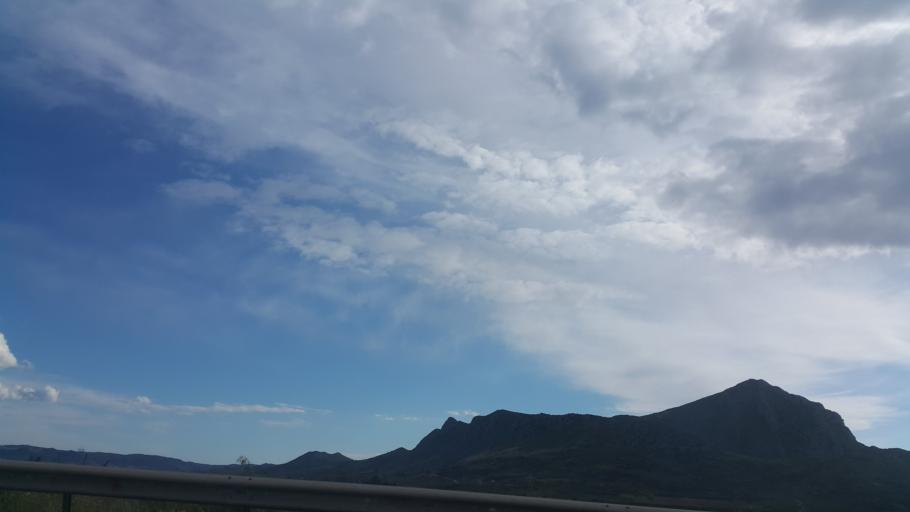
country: TR
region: Adana
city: Ceyhan
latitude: 36.9905
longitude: 35.7451
